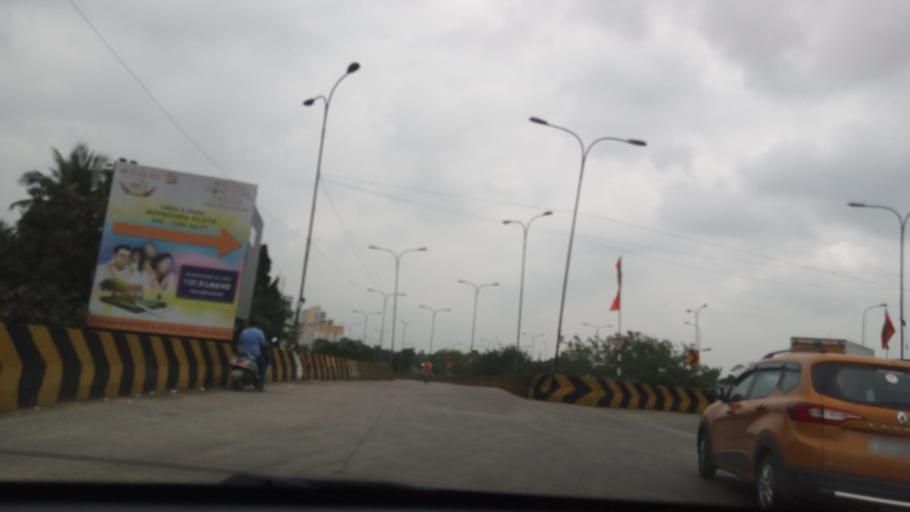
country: IN
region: Tamil Nadu
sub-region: Kancheepuram
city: Vandalur
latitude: 12.8927
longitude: 80.0862
